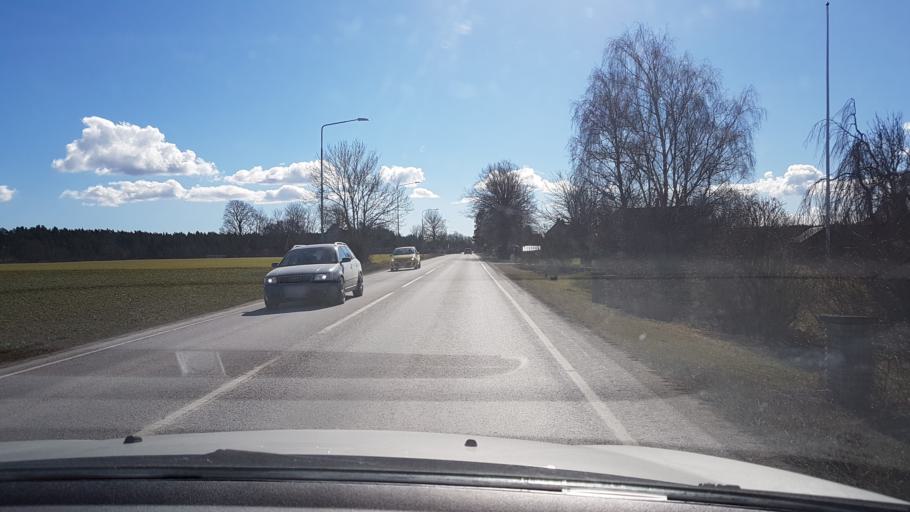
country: SE
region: Gotland
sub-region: Gotland
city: Visby
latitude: 57.5252
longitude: 18.4409
